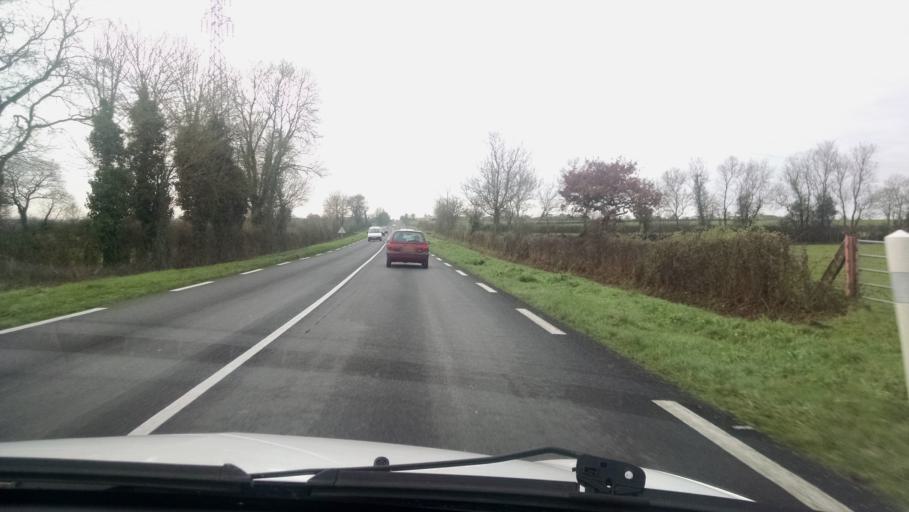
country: FR
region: Pays de la Loire
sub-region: Departement de Maine-et-Loire
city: Le Longeron
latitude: 47.0501
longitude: -1.0624
